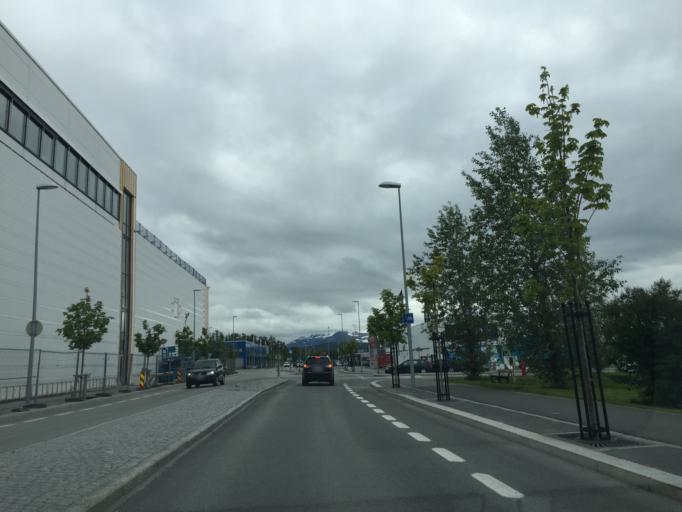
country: NO
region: Nordland
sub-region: Bodo
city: Bodo
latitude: 67.2781
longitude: 14.4186
